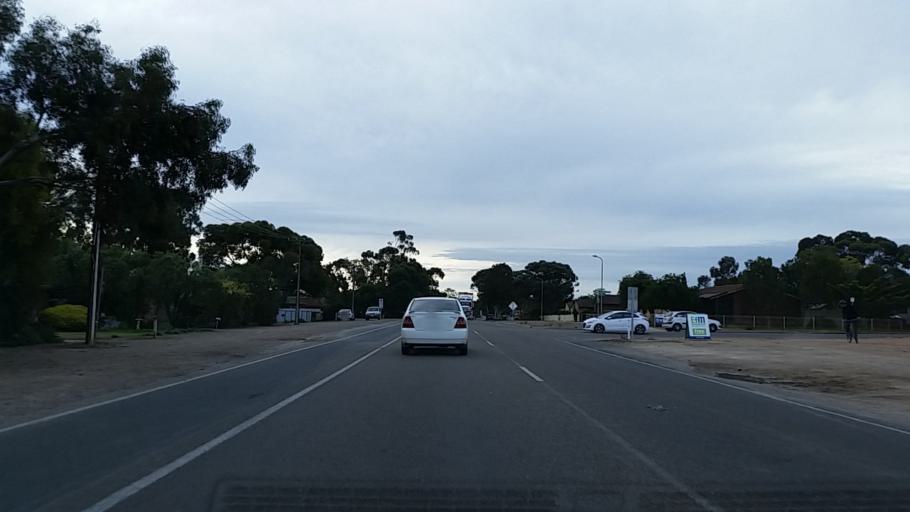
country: AU
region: South Australia
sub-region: Murray Bridge
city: Murray Bridge
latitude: -35.1431
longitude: 139.2857
